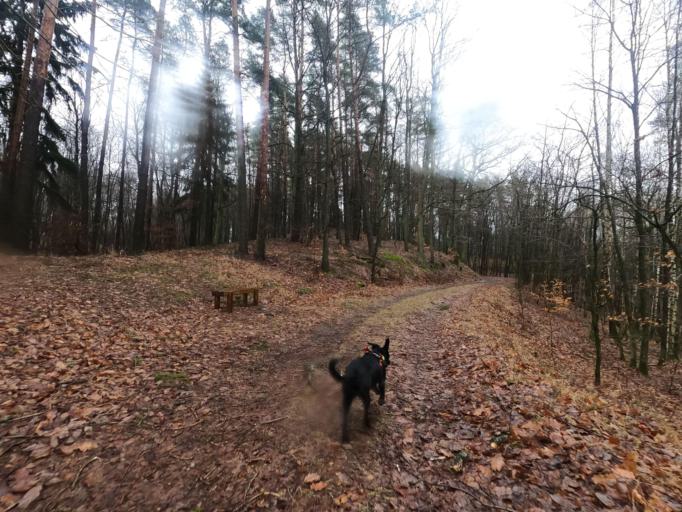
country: PL
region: Greater Poland Voivodeship
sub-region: Powiat pilski
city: Wyrzysk
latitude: 53.1274
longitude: 17.2532
